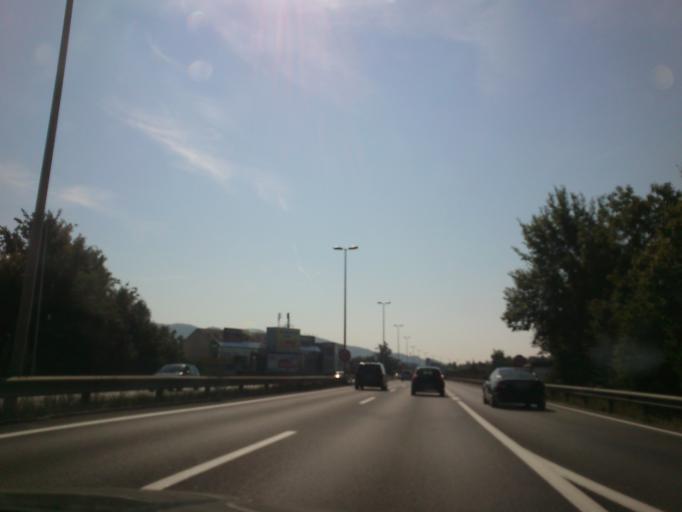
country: AT
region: Upper Austria
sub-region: Linz Stadt
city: Linz
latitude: 48.3174
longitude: 14.3024
